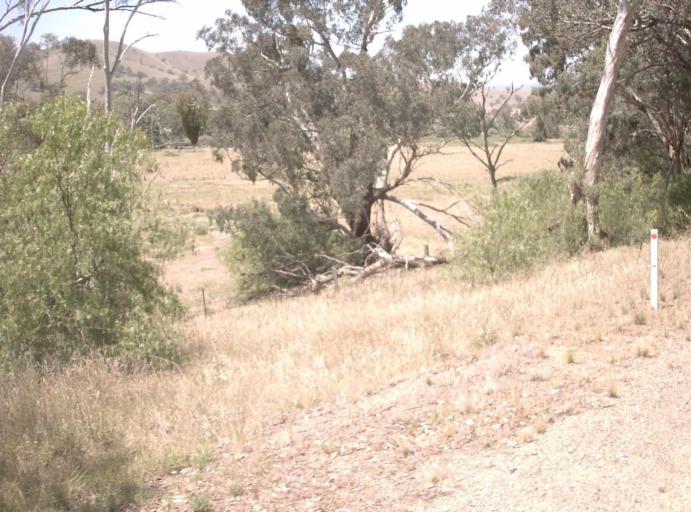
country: AU
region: Victoria
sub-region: East Gippsland
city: Bairnsdale
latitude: -37.2123
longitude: 147.7174
